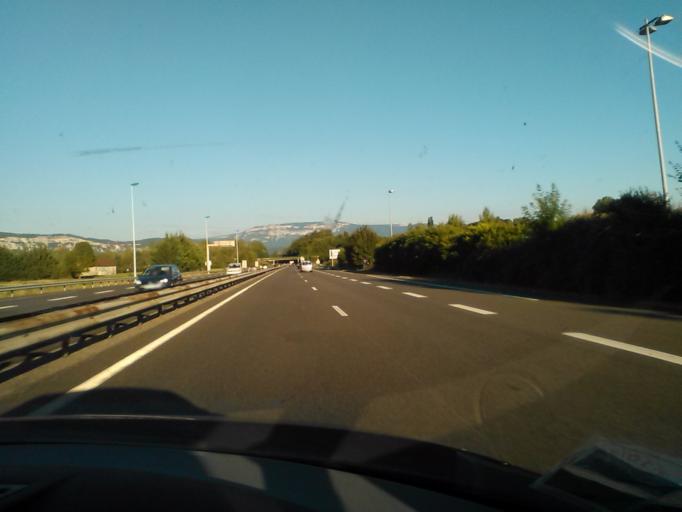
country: FR
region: Rhone-Alpes
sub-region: Departement de l'Isere
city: Romagnieu
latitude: 45.5770
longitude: 5.6358
